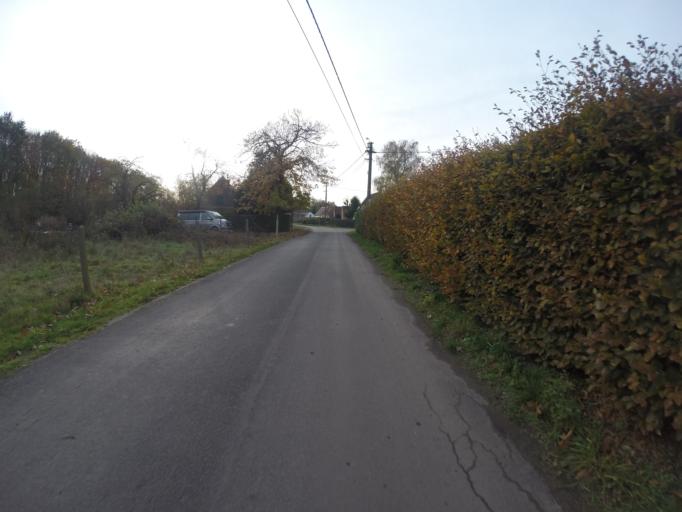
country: BE
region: Flanders
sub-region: Provincie Oost-Vlaanderen
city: Aalter
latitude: 51.0711
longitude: 3.4958
